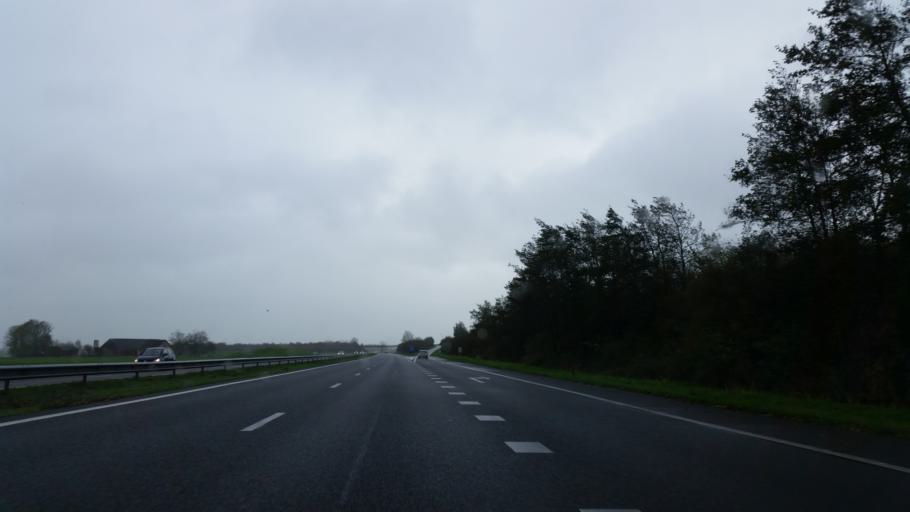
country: NL
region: Friesland
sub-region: Gemeente Boarnsterhim
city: Reduzum
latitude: 53.1178
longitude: 5.8095
